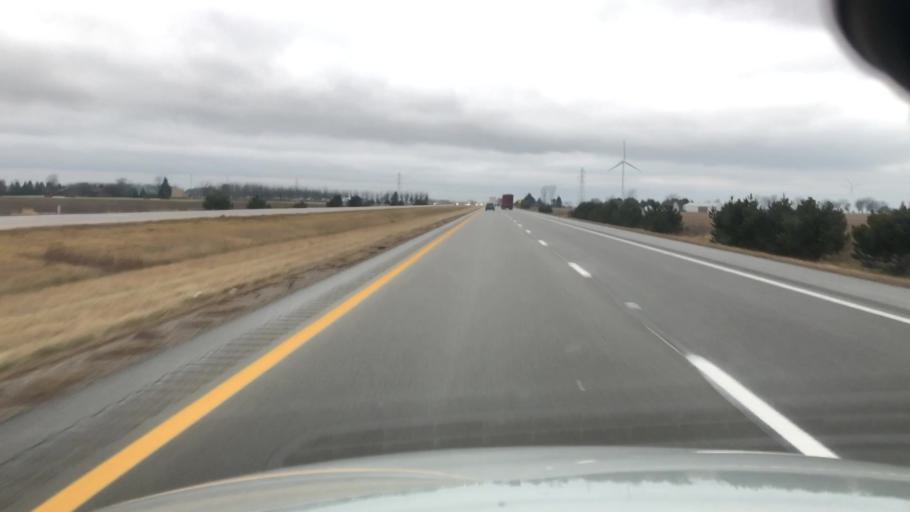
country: US
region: Ohio
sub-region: Van Wert County
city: Convoy
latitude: 40.9203
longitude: -84.6771
